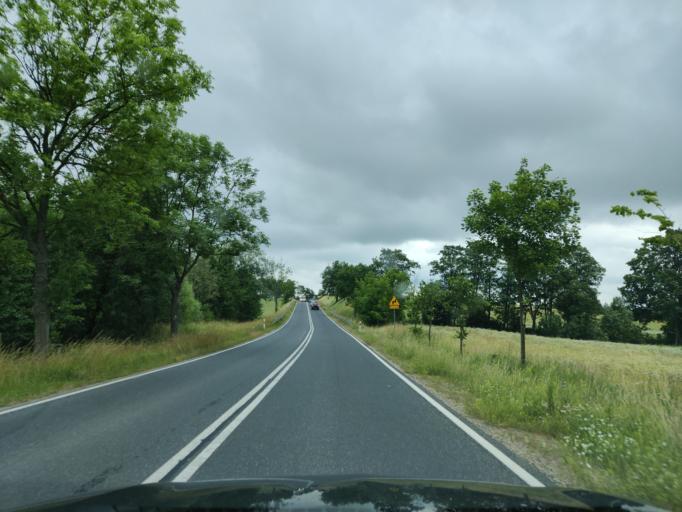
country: PL
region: Warmian-Masurian Voivodeship
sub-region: Powiat gizycki
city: Ryn
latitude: 53.9096
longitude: 21.4335
